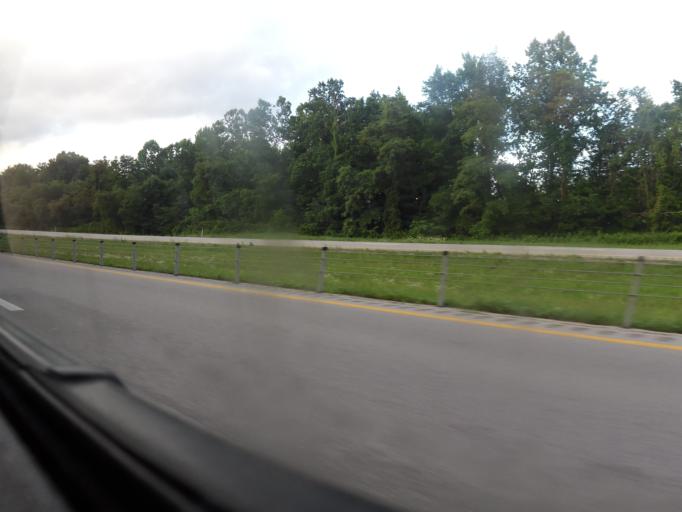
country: US
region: Kentucky
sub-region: Rockcastle County
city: Mount Vernon
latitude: 37.3107
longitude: -84.2908
